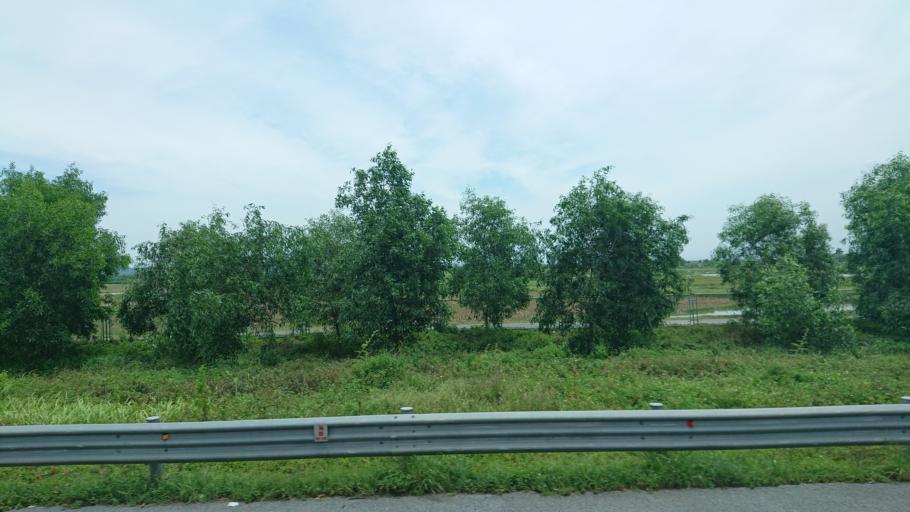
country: VN
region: Hai Phong
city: Nui Doi
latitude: 20.7658
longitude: 106.6534
